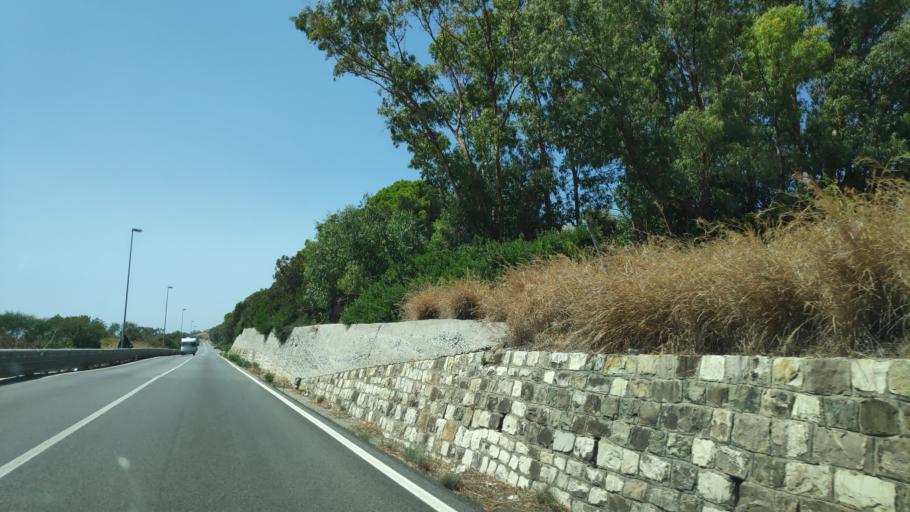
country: IT
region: Calabria
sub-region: Provincia di Reggio Calabria
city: Africo Nuovo
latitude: 38.0119
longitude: 16.1313
